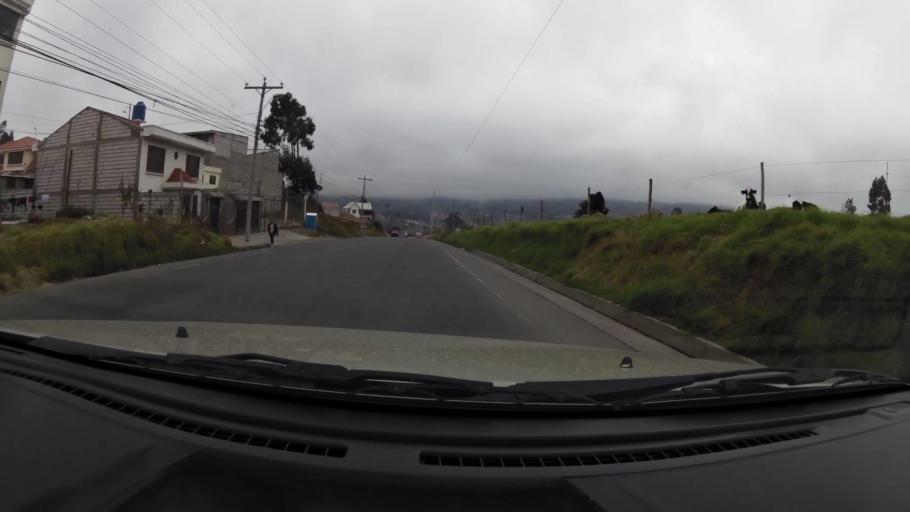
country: EC
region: Canar
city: Canar
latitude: -2.5394
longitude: -78.9325
